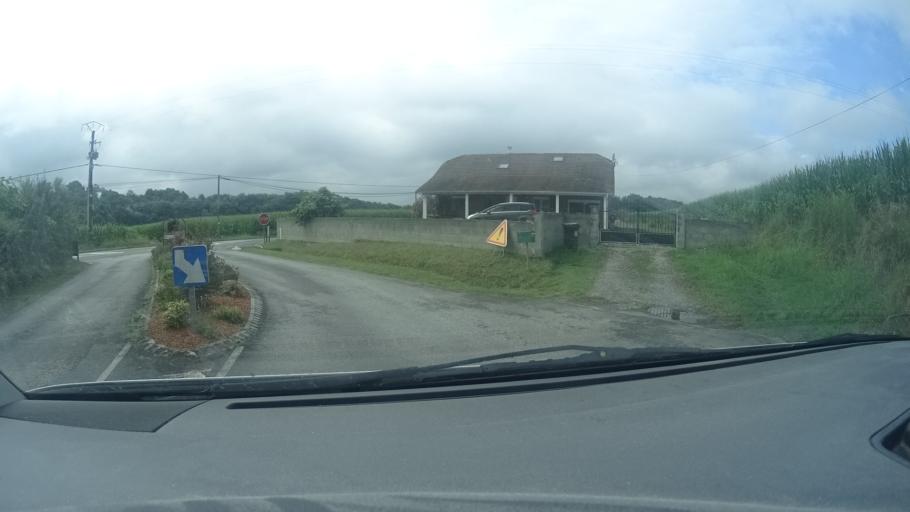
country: FR
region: Aquitaine
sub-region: Departement des Pyrenees-Atlantiques
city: Orthez
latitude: 43.4851
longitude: -0.7010
